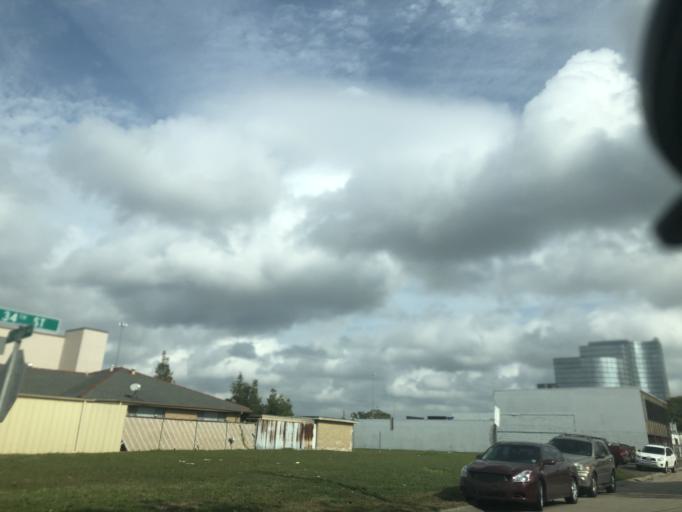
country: US
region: Louisiana
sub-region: Jefferson Parish
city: Metairie
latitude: 29.9948
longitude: -90.1575
